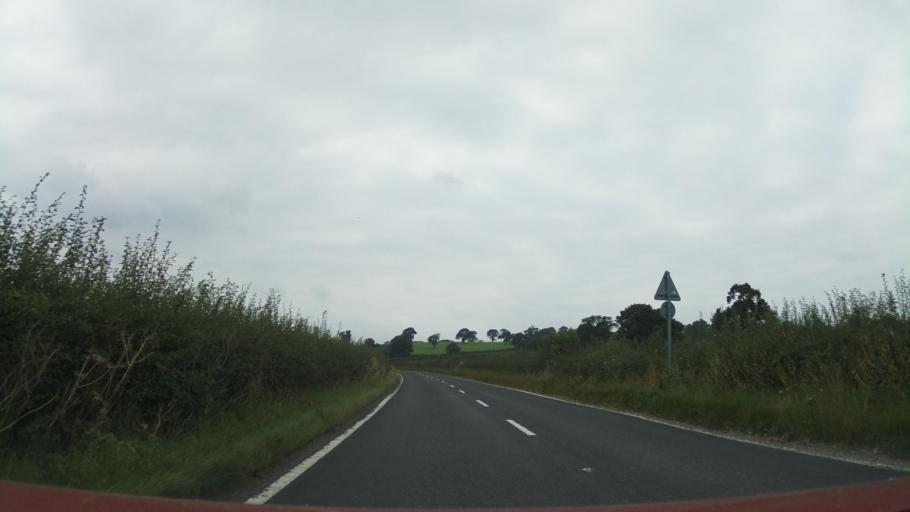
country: GB
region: England
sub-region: Derbyshire
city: Wirksworth
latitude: 53.0225
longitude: -1.5483
